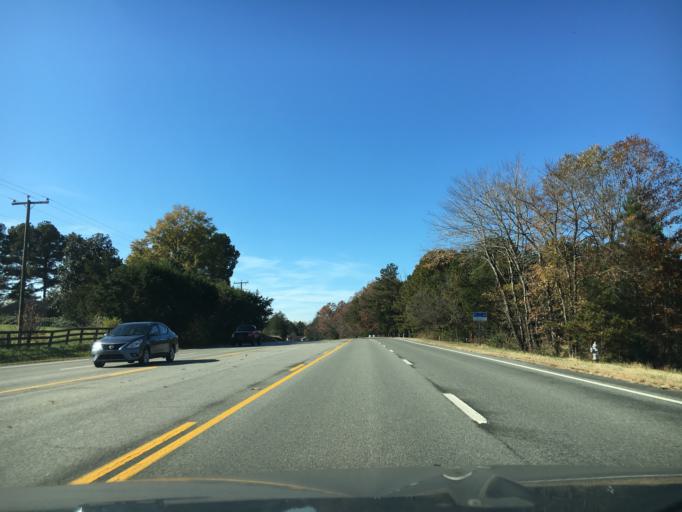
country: US
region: Virginia
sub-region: Cumberland County
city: Cumberland
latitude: 37.4872
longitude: -78.2608
